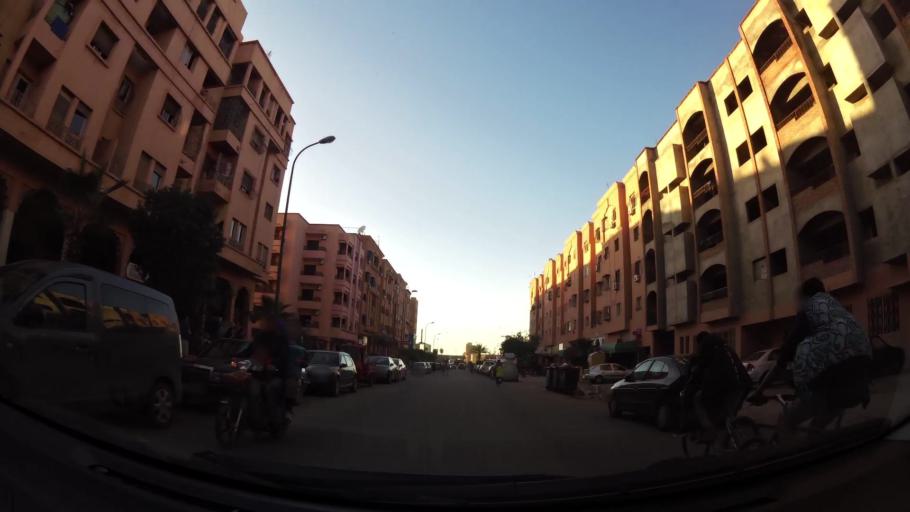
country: MA
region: Marrakech-Tensift-Al Haouz
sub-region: Marrakech
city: Marrakesh
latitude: 31.6224
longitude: -8.0285
